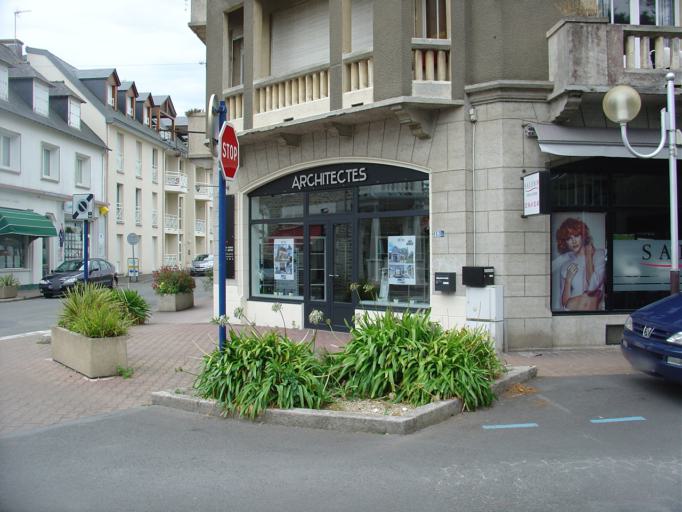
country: FR
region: Brittany
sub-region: Departement des Cotes-d'Armor
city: Saint-Cast-le-Guildo
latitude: 48.6323
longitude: -2.2559
